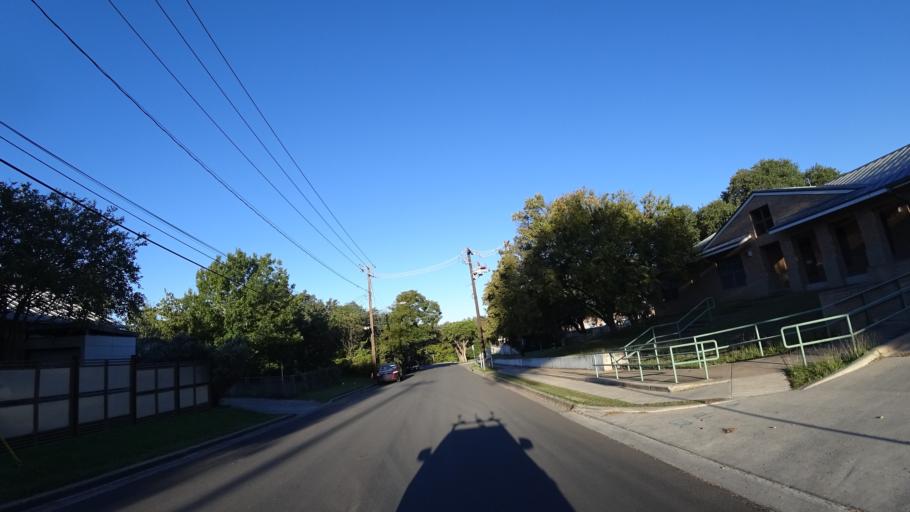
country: US
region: Texas
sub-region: Travis County
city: Austin
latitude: 30.2497
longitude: -97.7525
